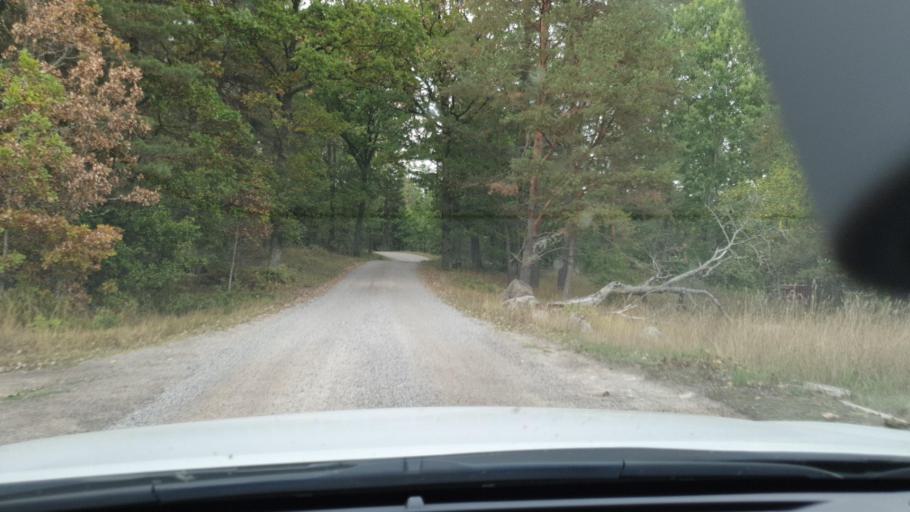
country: SE
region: Kalmar
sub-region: Vasterviks Kommun
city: Vaestervik
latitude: 57.7292
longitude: 16.4794
